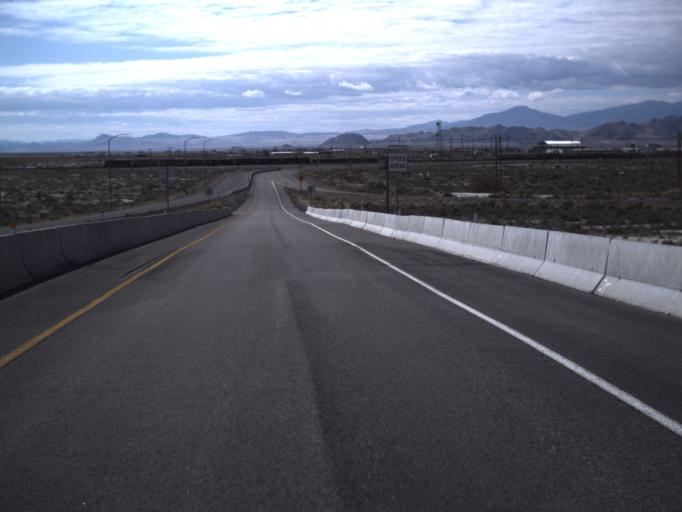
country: US
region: Utah
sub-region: Tooele County
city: Wendover
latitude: 40.7456
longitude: -114.0174
